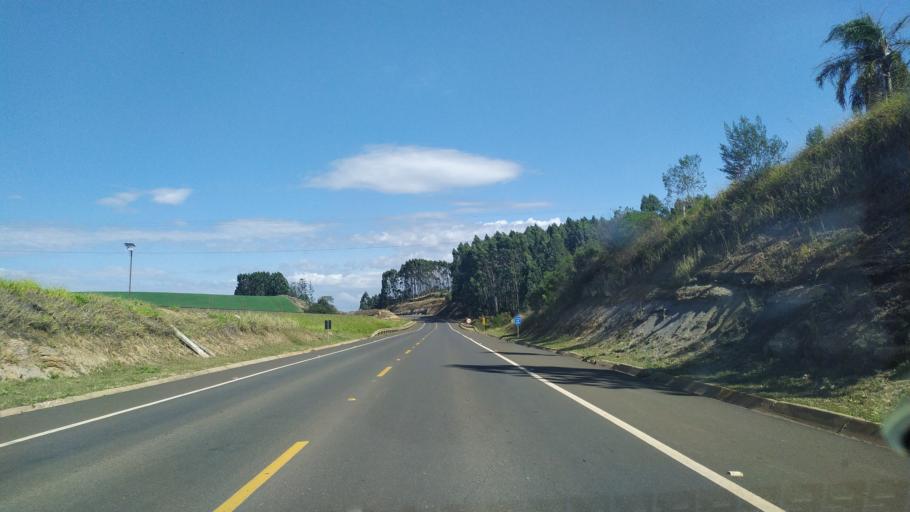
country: BR
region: Parana
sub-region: Ortigueira
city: Ortigueira
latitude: -24.2886
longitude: -50.8149
